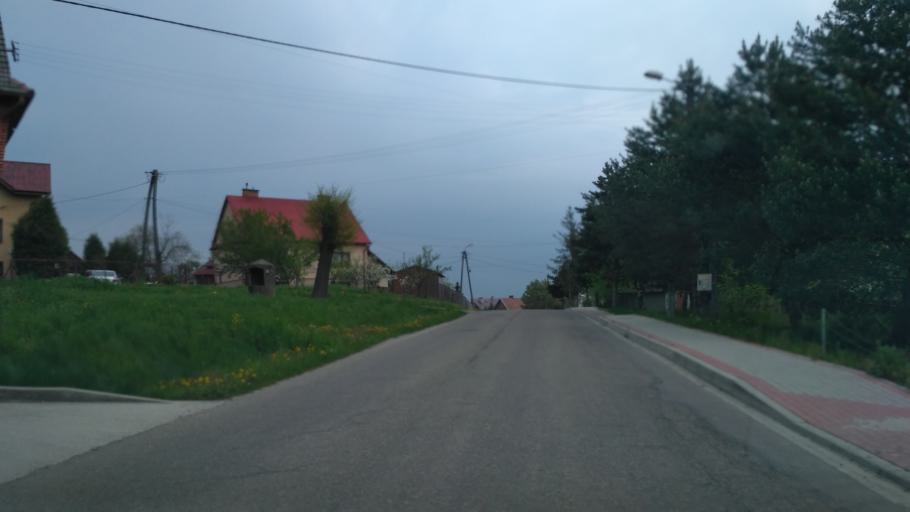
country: PL
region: Lesser Poland Voivodeship
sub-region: Powiat tarnowski
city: Skrzyszow
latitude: 49.9547
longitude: 21.0357
